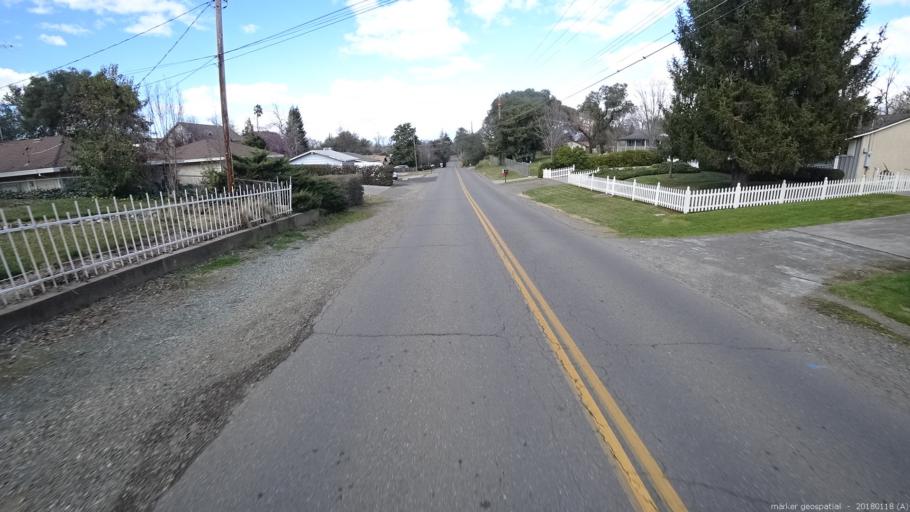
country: US
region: California
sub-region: Sacramento County
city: Orangevale
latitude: 38.6933
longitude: -121.2065
